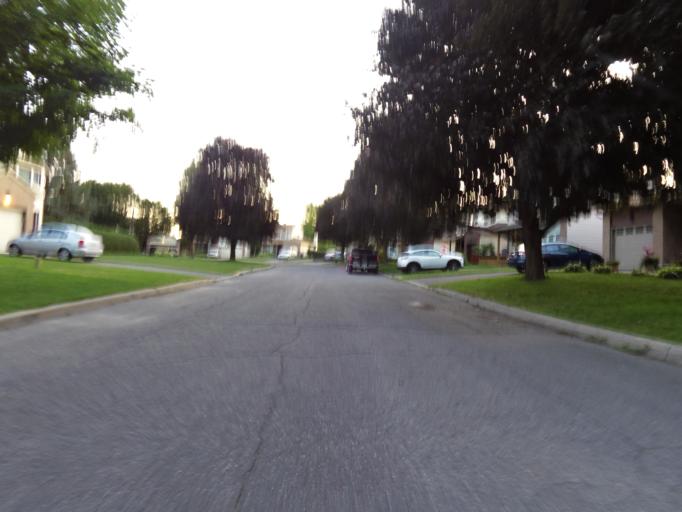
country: CA
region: Quebec
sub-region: Outaouais
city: Gatineau
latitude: 45.4680
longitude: -75.4945
